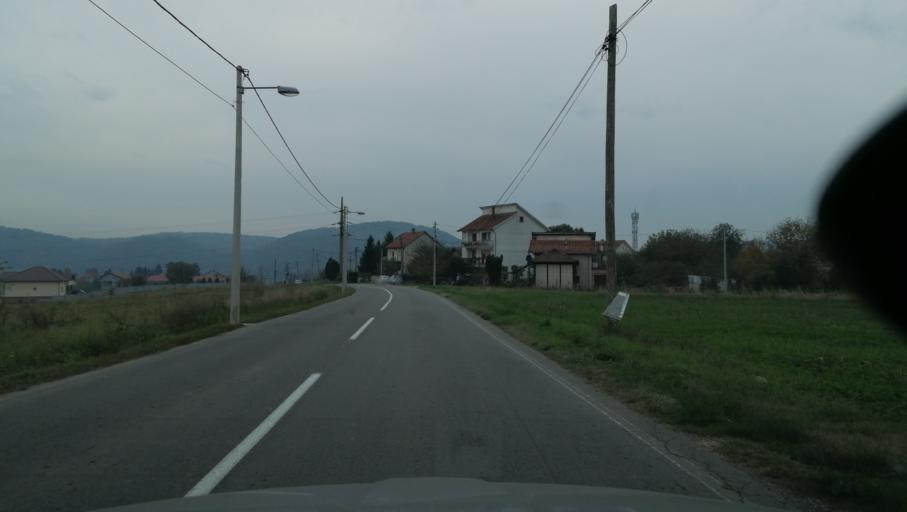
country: RS
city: Rusanj
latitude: 44.6748
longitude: 20.5042
